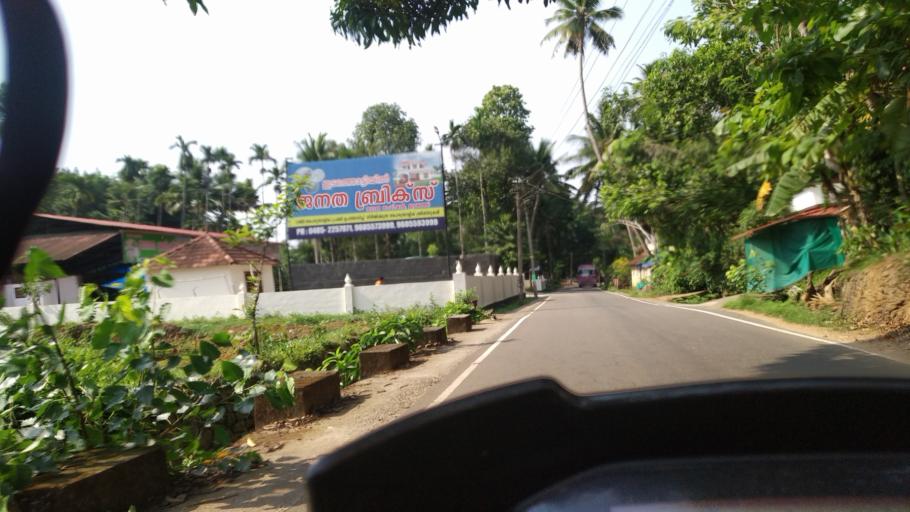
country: IN
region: Kerala
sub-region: Ernakulam
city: Piravam
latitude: 9.8405
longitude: 76.5356
